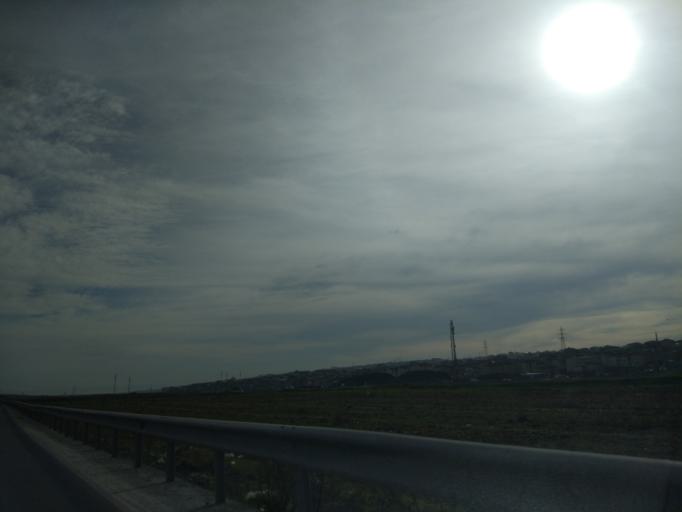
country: TR
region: Istanbul
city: Esenyurt
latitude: 41.0461
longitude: 28.7042
